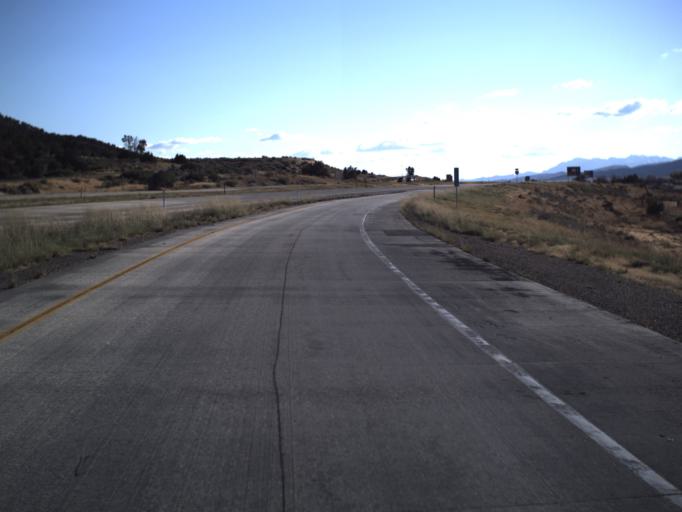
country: US
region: Utah
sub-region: Juab County
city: Nephi
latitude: 39.7080
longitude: -111.8183
